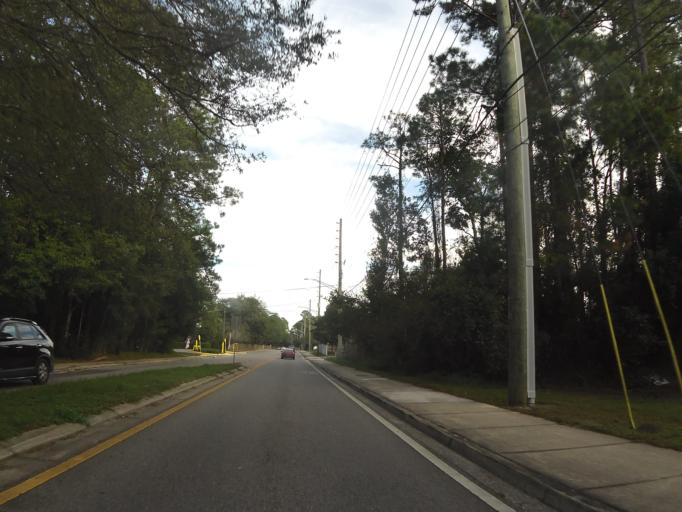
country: US
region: Florida
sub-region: Saint Johns County
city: Fruit Cove
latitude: 30.1596
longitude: -81.6195
